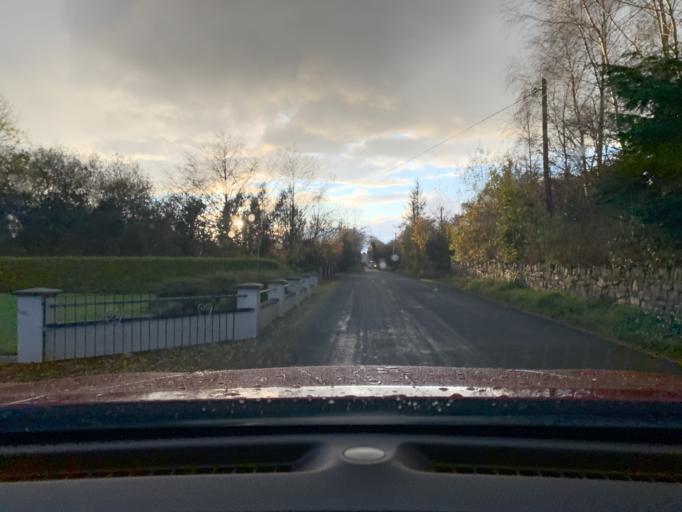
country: IE
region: Connaught
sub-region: Sligo
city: Sligo
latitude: 54.3128
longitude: -8.4911
